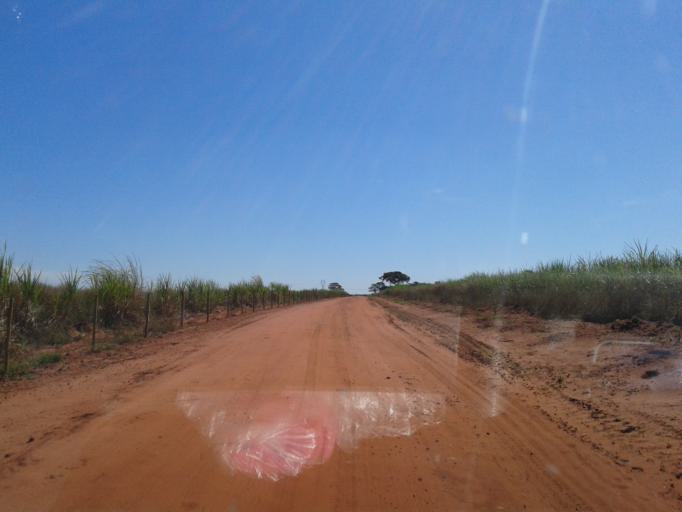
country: BR
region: Minas Gerais
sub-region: Santa Vitoria
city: Santa Vitoria
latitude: -19.0231
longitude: -50.3661
